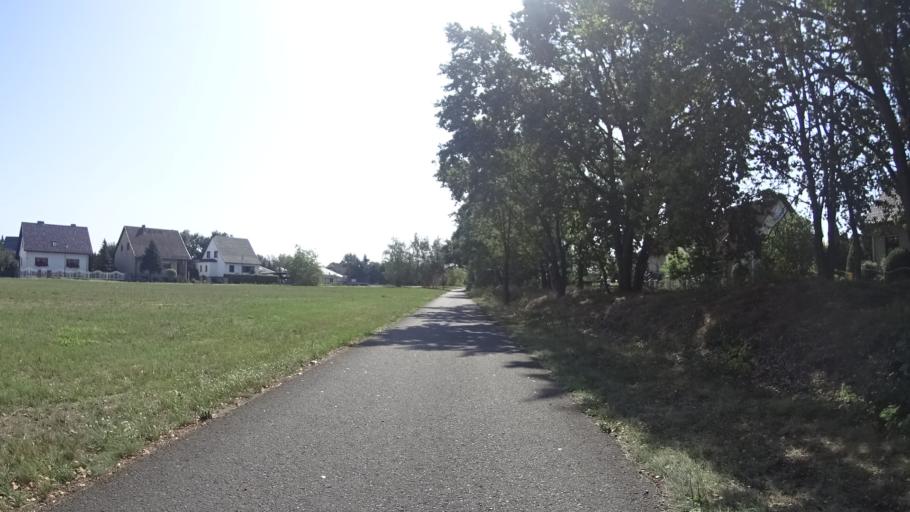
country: DE
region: Brandenburg
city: Cottbus
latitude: 51.7933
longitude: 14.3020
